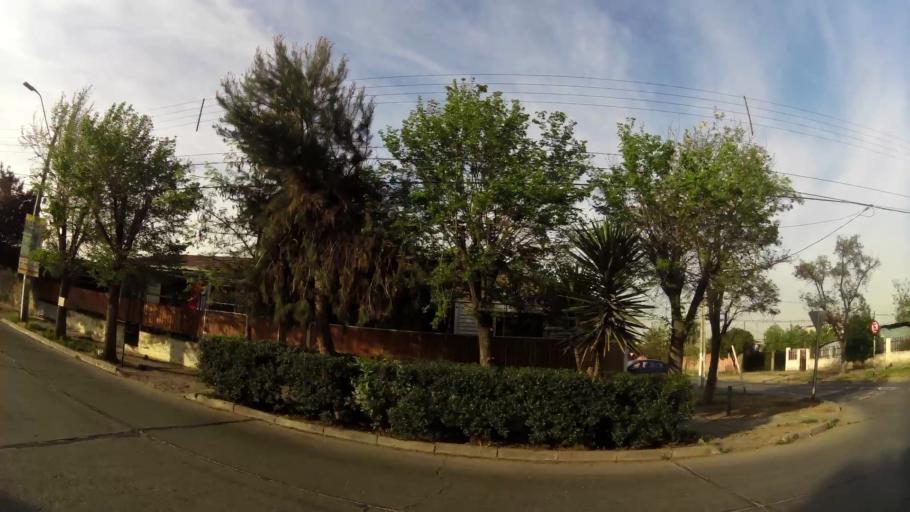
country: CL
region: Santiago Metropolitan
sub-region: Provincia de Santiago
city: La Pintana
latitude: -33.5332
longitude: -70.6722
